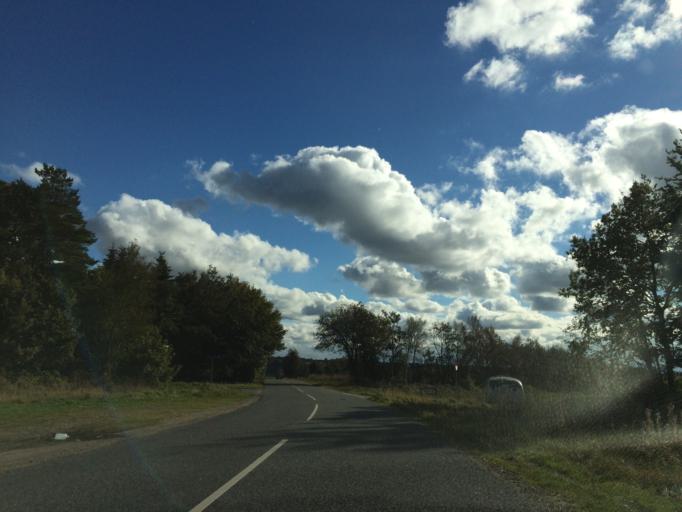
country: DK
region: Central Jutland
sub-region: Skanderborg Kommune
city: Ry
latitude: 56.1961
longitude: 9.7599
